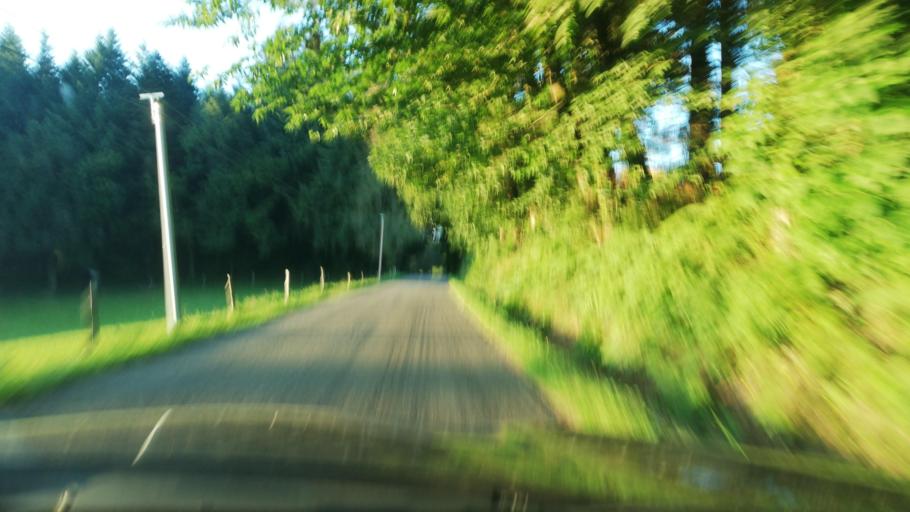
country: FR
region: Midi-Pyrenees
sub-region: Departement du Lot
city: Saint-Cere
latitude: 44.8861
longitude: 2.0281
